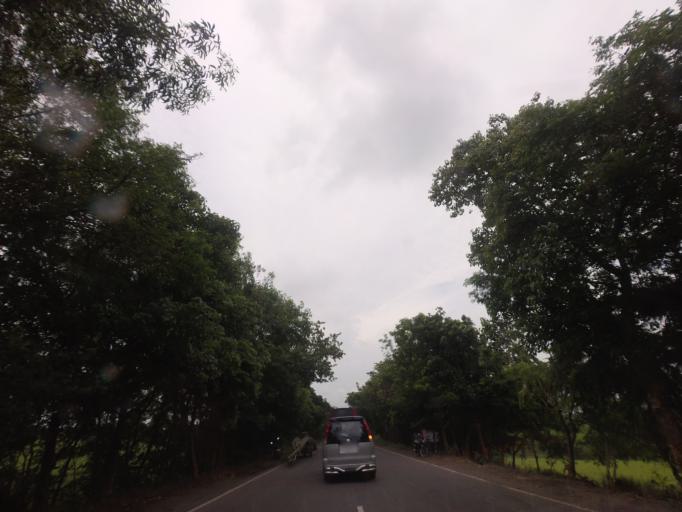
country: BD
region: Khulna
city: Kalia
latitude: 23.2808
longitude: 89.7971
